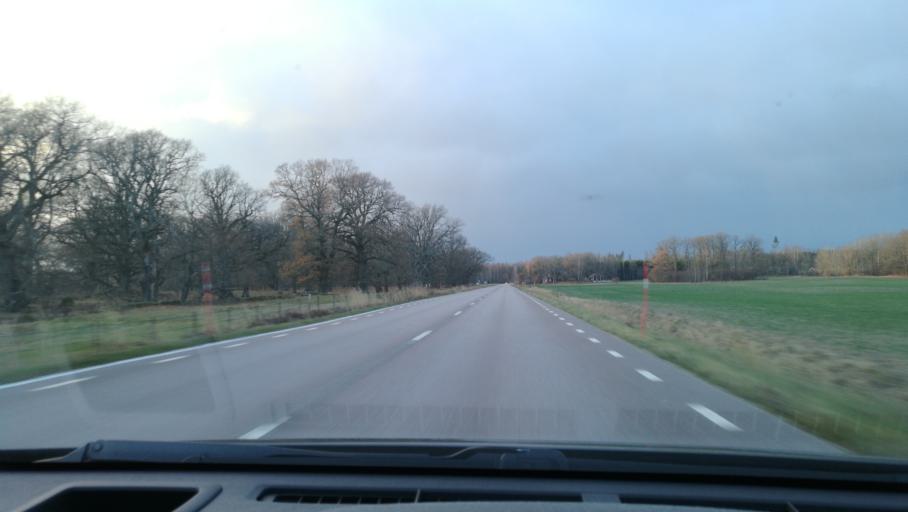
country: SE
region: Soedermanland
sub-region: Vingakers Kommun
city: Vingaker
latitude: 59.1615
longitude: 16.0019
